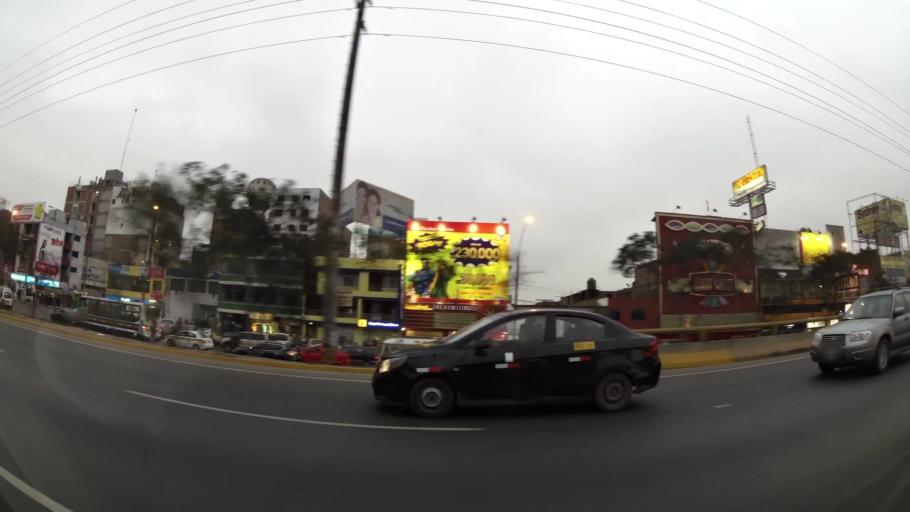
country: PE
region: Lima
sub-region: Lima
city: Independencia
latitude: -11.9922
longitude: -77.0638
